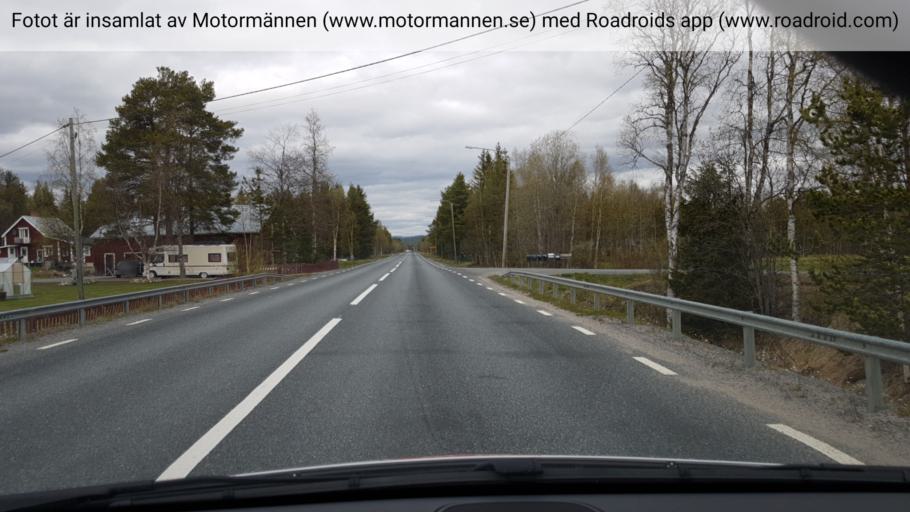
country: SE
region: Vaesterbotten
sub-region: Sorsele Kommun
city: Sorsele
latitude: 65.5118
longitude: 17.5399
